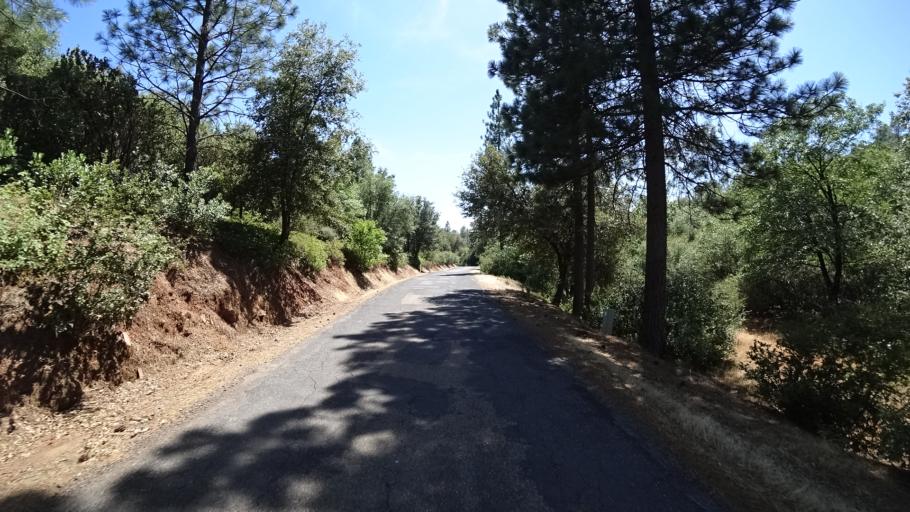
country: US
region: California
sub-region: Calaveras County
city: Murphys
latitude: 38.1745
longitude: -120.4494
